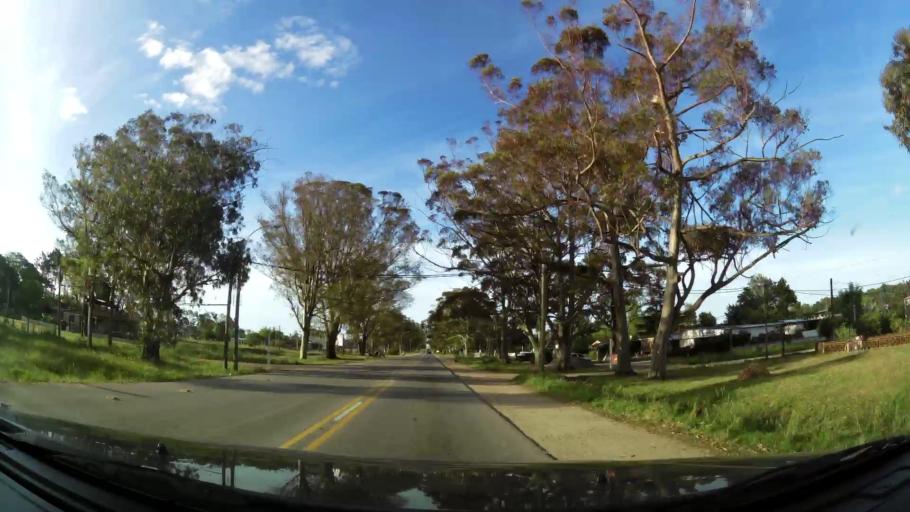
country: UY
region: Canelones
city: Atlantida
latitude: -34.7694
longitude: -55.8417
